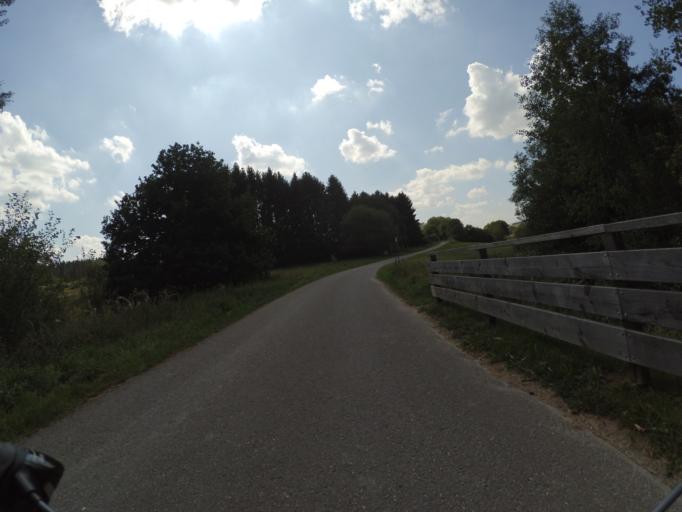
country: DE
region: Rheinland-Pfalz
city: Morbach
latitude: 49.8350
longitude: 7.1655
